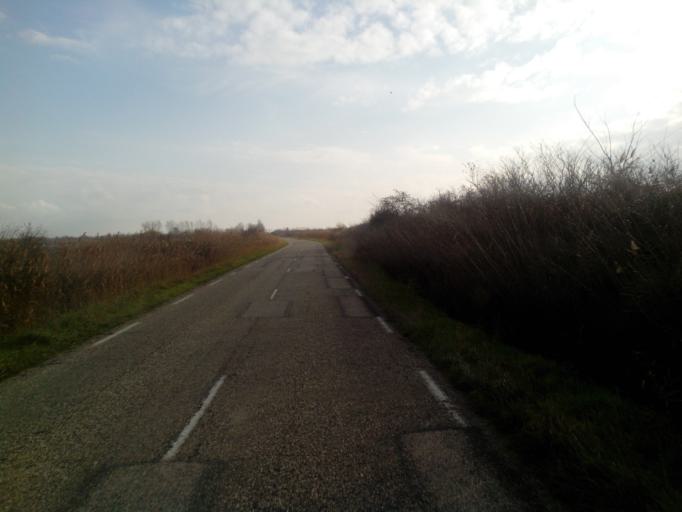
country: FR
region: Languedoc-Roussillon
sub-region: Departement du Gard
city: Saint-Gilles
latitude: 43.5915
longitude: 4.4935
